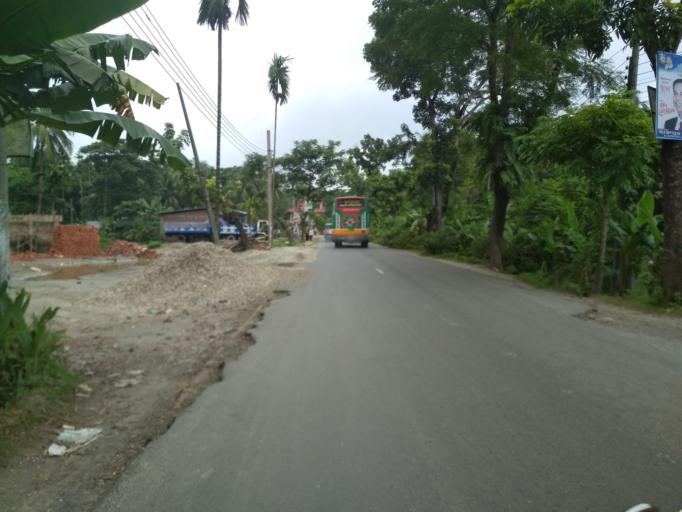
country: BD
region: Chittagong
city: Lakshmipur
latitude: 22.9466
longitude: 90.8101
